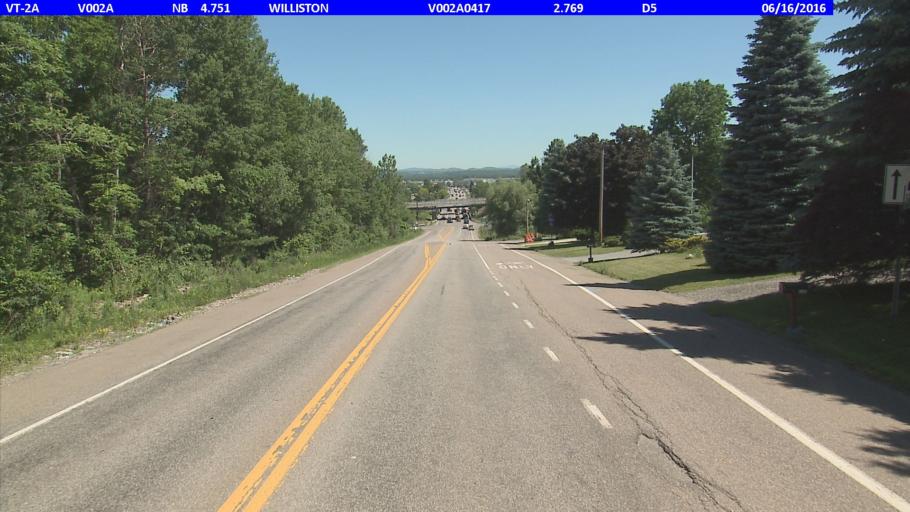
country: US
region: Vermont
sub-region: Chittenden County
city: Williston
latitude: 44.4368
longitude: -73.1164
